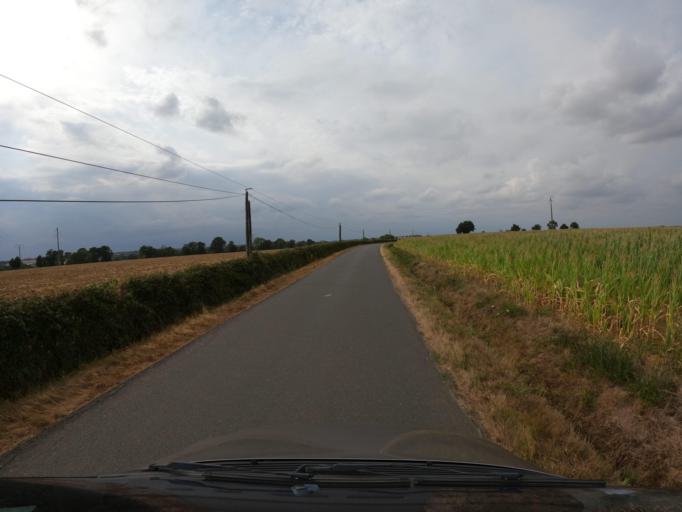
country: FR
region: Pays de la Loire
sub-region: Departement de Maine-et-Loire
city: Saint-Christophe-du-Bois
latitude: 47.0307
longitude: -0.9564
